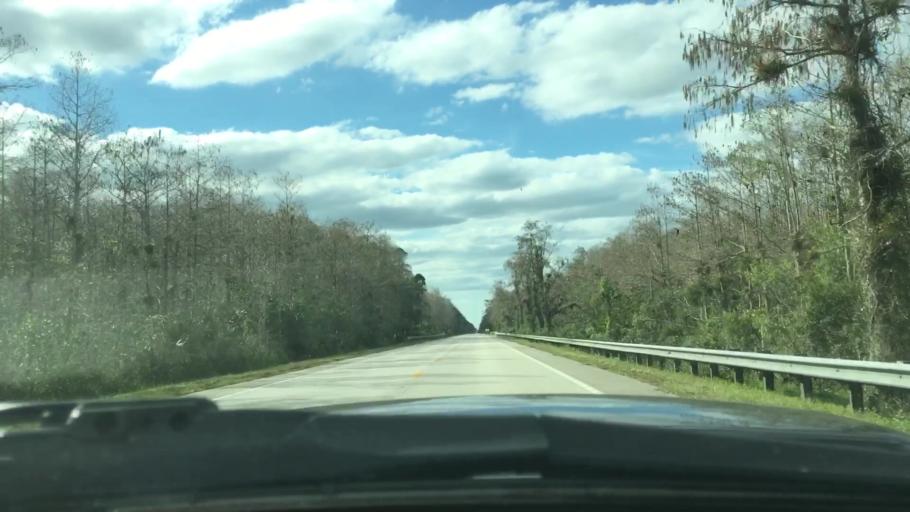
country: US
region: Florida
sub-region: Miami-Dade County
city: Kendall West
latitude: 25.8533
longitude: -80.9996
